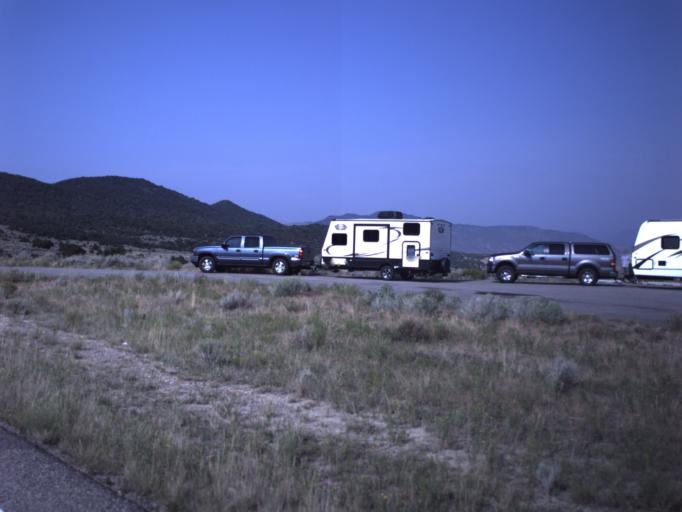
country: US
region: Utah
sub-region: Daggett County
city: Manila
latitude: 40.9665
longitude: -109.4665
